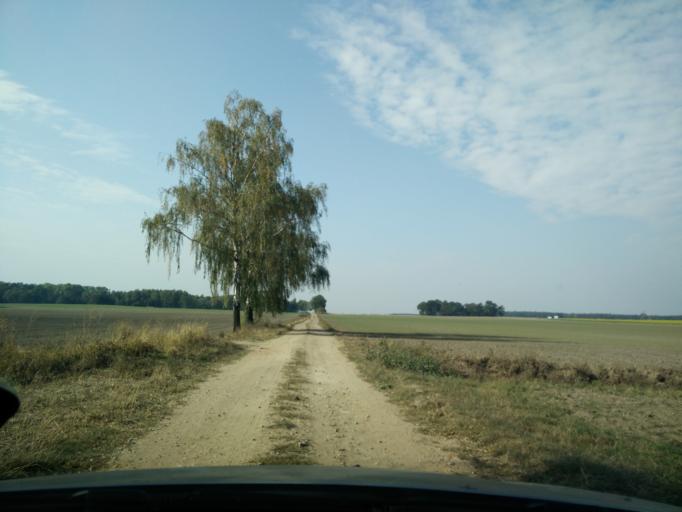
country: PL
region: Greater Poland Voivodeship
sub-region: Powiat sredzki
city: Sroda Wielkopolska
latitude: 52.3059
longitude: 17.2668
